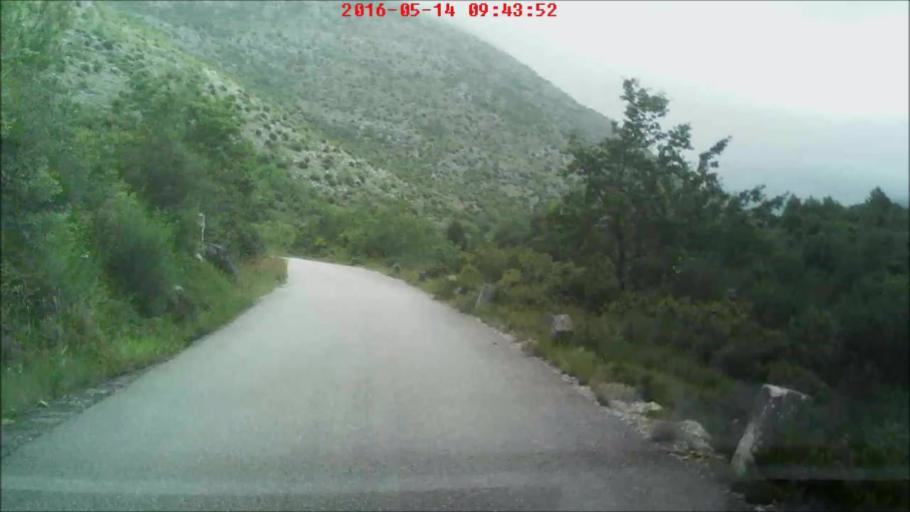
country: HR
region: Dubrovacko-Neretvanska
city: Podgora
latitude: 42.7857
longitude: 17.9061
